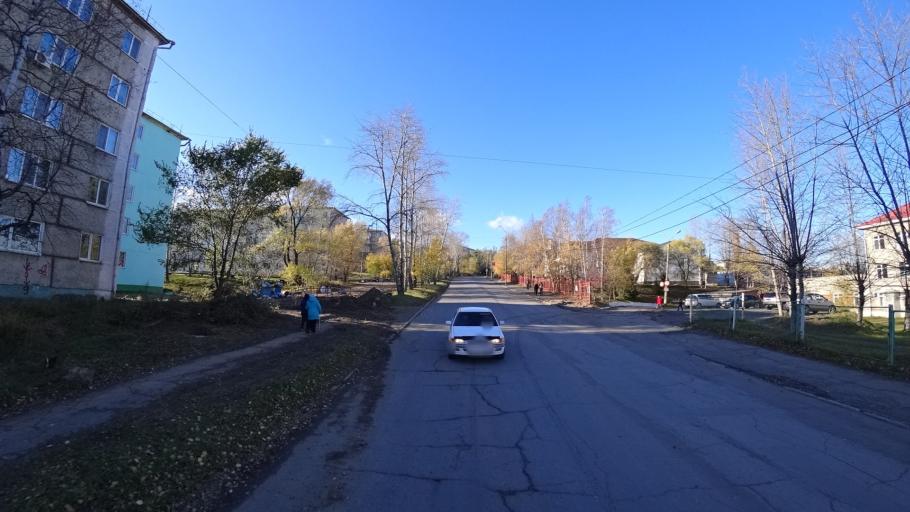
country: RU
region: Khabarovsk Krai
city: Amursk
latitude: 50.2337
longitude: 136.9071
